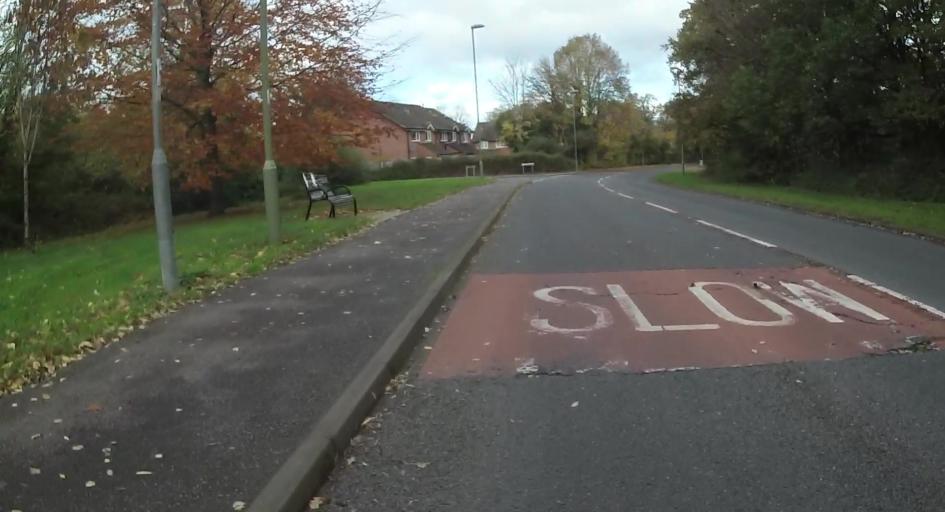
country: GB
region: England
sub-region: Hampshire
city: Old Basing
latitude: 51.2912
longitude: -1.0539
